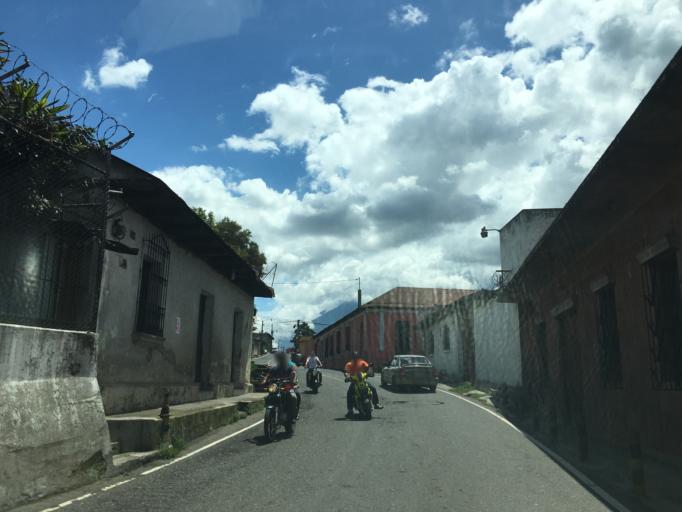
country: GT
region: Sacatepequez
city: Ciudad Vieja
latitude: 14.5250
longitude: -90.7659
